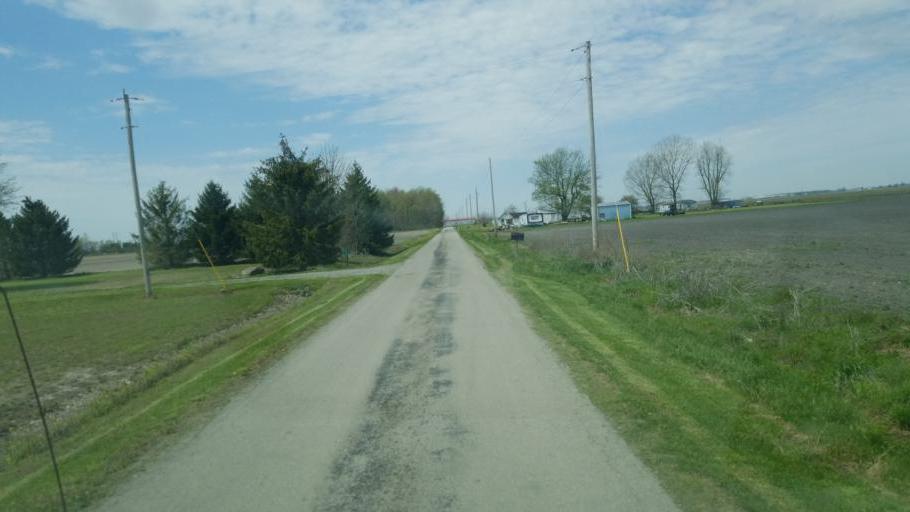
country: US
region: Ohio
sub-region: Hardin County
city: Ada
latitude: 40.6562
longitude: -83.7611
